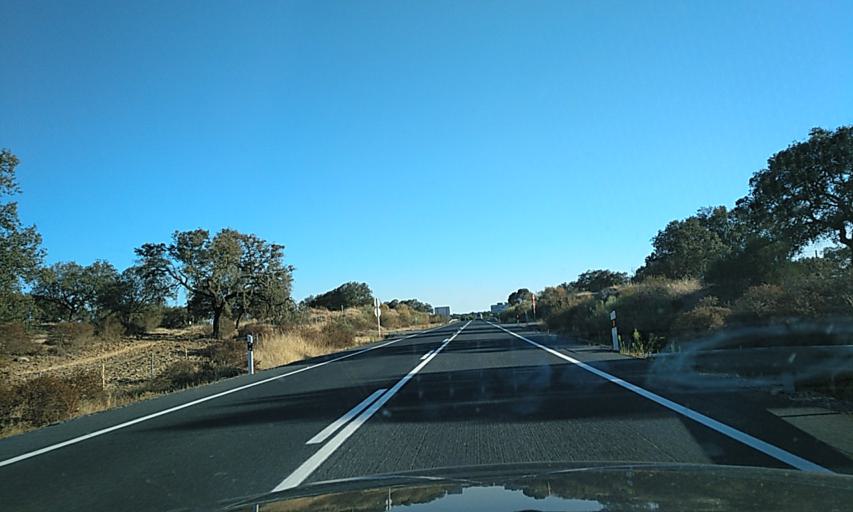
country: ES
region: Andalusia
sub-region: Provincia de Huelva
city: San Bartolome de la Torre
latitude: 37.4563
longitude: -7.1262
